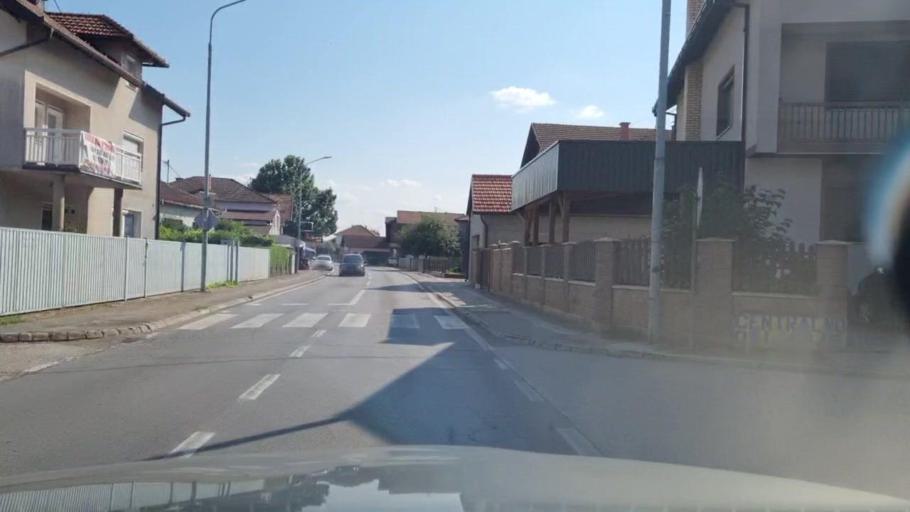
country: BA
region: Federation of Bosnia and Herzegovina
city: Odzak
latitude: 45.0099
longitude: 18.3274
